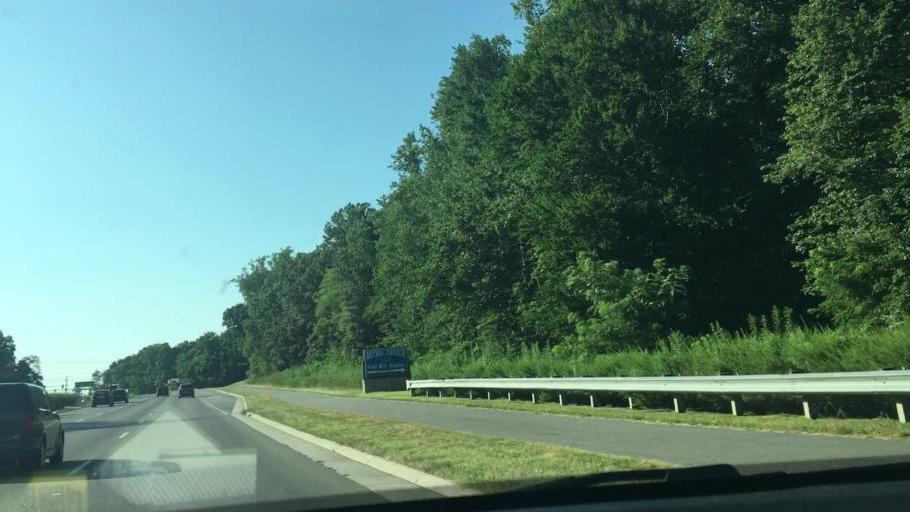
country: US
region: Virginia
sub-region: Prince William County
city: Dale City
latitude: 38.6616
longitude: -77.3260
